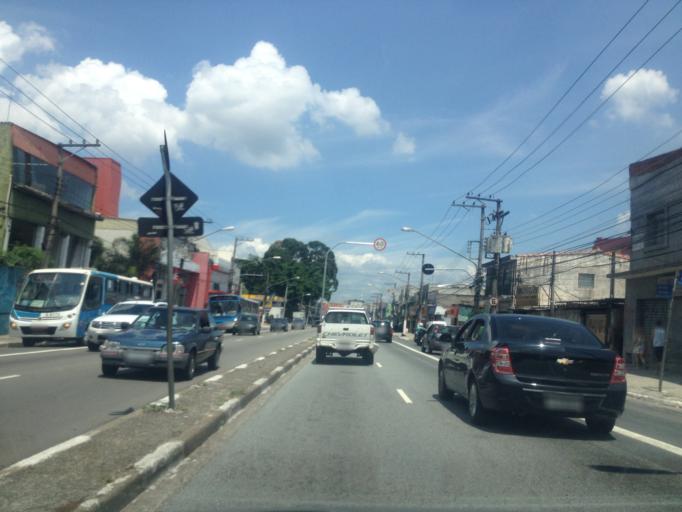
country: BR
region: Sao Paulo
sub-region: Diadema
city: Diadema
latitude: -23.6771
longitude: -46.6813
